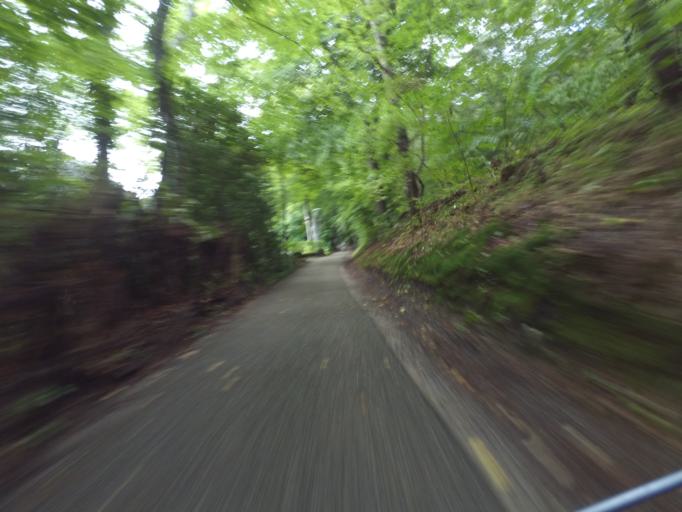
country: NL
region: North Holland
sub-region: Gemeente Alkmaar
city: Alkmaar
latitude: 52.6878
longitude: 4.7001
